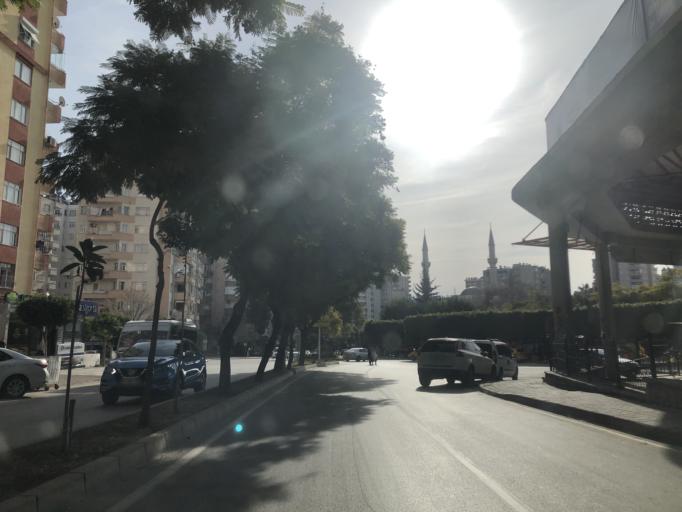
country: TR
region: Adana
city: Adana
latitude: 37.0516
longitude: 35.2840
